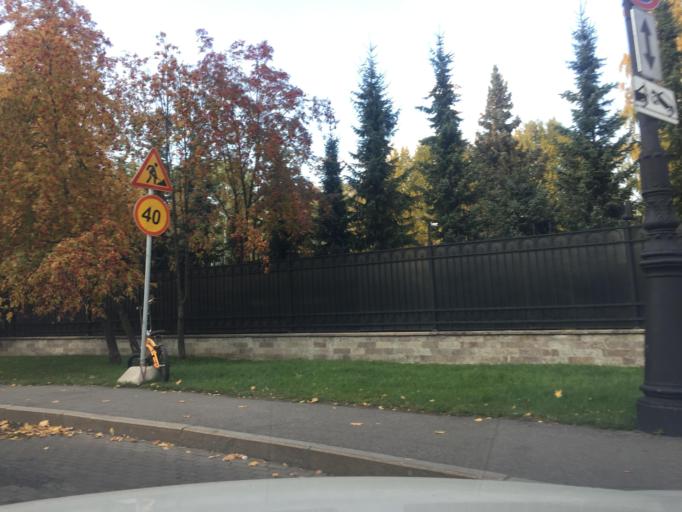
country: RU
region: St.-Petersburg
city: Novaya Derevnya
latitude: 59.9768
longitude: 30.2762
